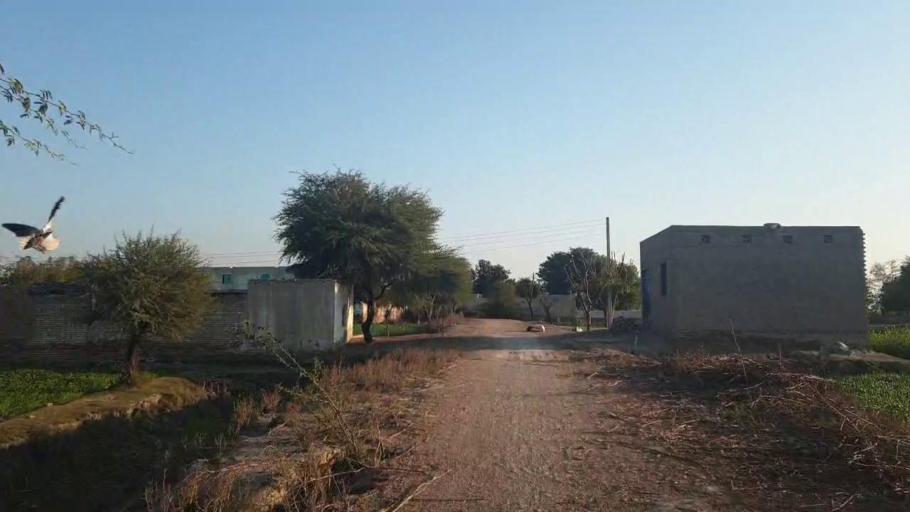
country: PK
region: Sindh
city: Khadro
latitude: 26.0692
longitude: 68.6877
